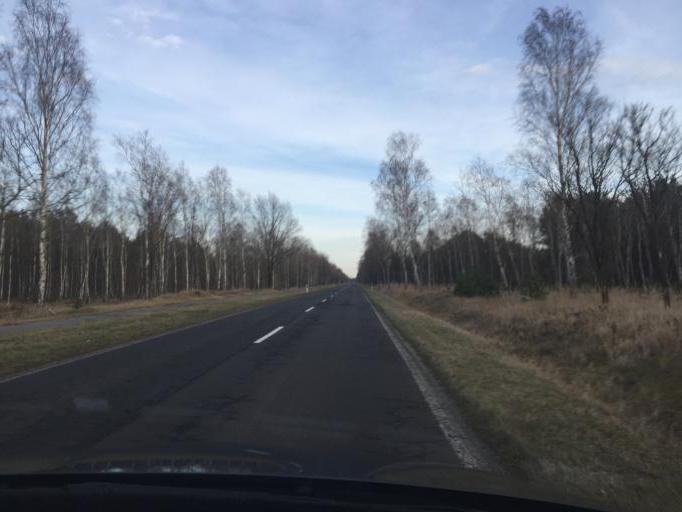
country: DE
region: Brandenburg
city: Forst
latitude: 51.7483
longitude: 14.6884
